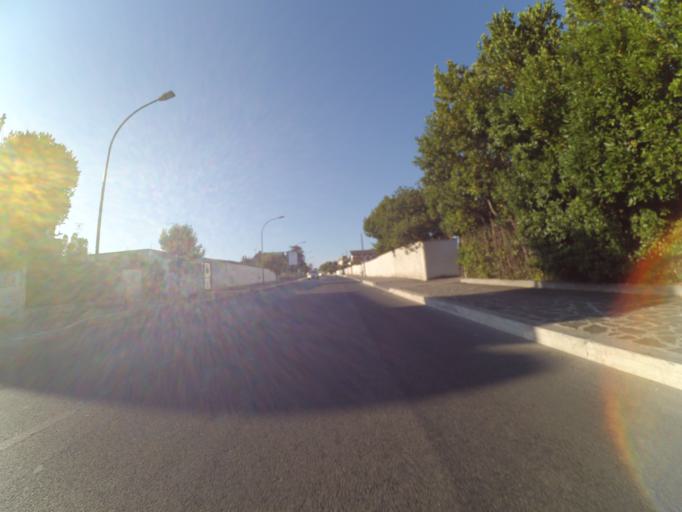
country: IT
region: Latium
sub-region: Provincia di Latina
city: San Felice Circeo
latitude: 41.2476
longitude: 13.0930
